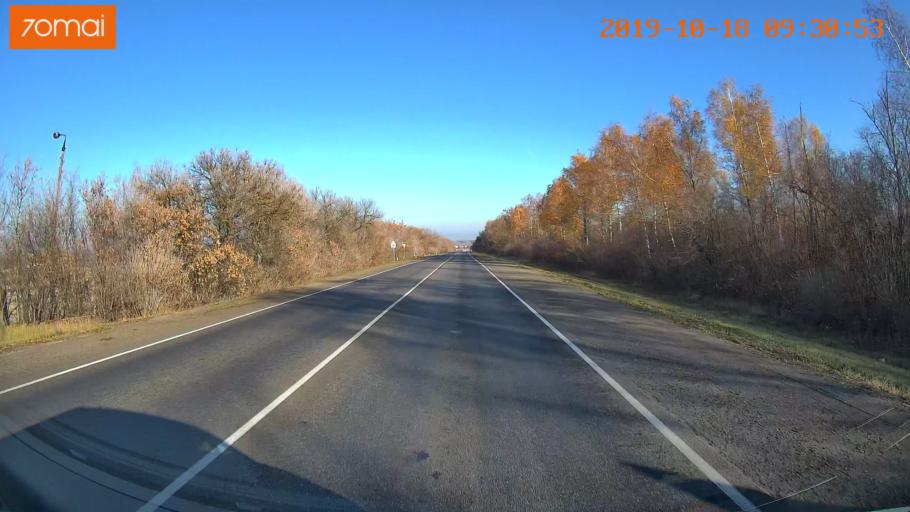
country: RU
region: Tula
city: Yefremov
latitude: 53.1437
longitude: 38.1590
